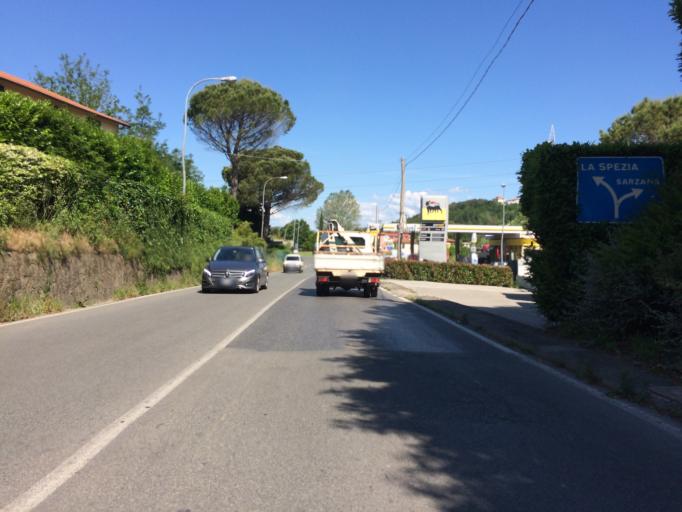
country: IT
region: Tuscany
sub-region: Provincia di Massa-Carrara
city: Borghetto-Melara
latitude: 44.1023
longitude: 9.9792
